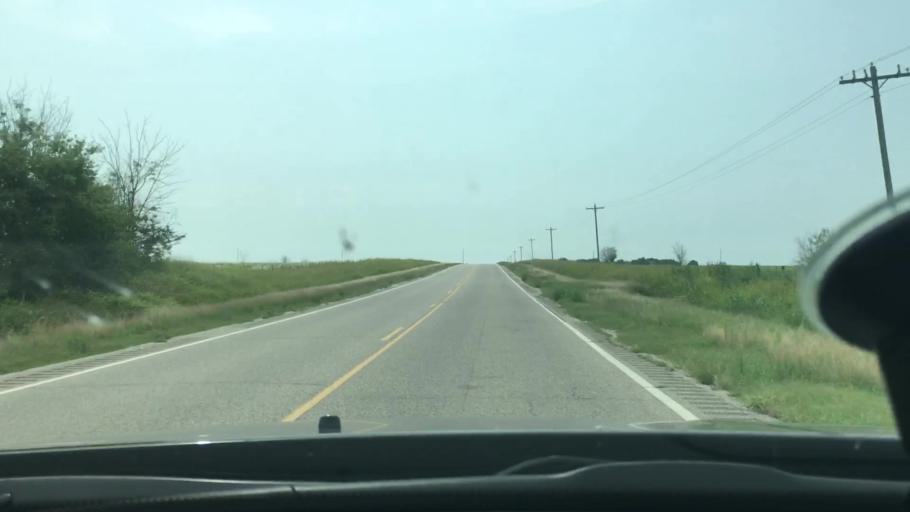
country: US
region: Oklahoma
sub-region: Marshall County
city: Kingston
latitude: 34.0205
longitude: -96.7611
